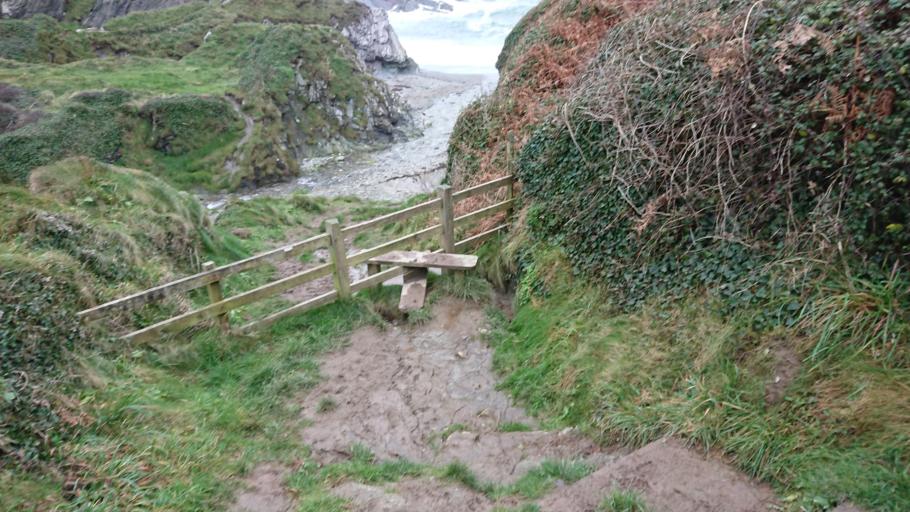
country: GB
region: England
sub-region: Cornwall
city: Fowey
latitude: 50.3324
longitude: -4.5781
